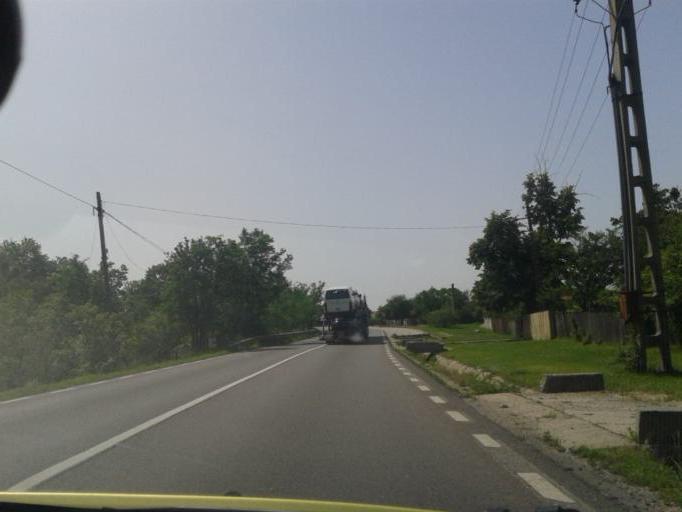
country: RO
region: Arges
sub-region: Comuna Cotmeana
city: Cotmeana
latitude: 44.9857
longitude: 24.6479
